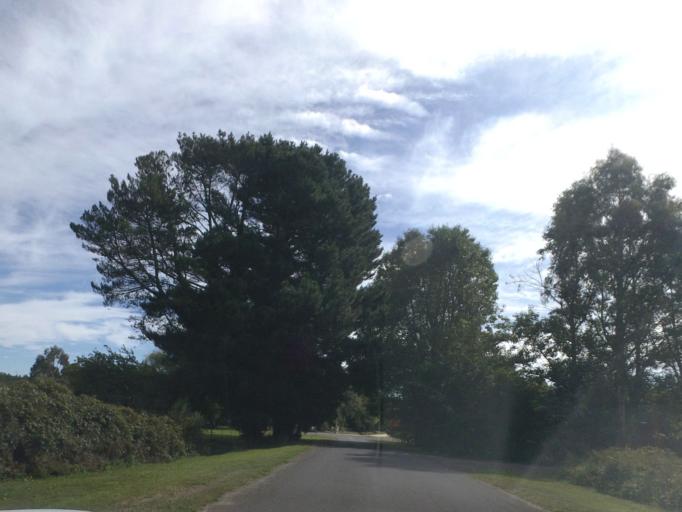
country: AU
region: Victoria
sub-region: Mount Alexander
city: Castlemaine
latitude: -37.3910
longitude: 144.2589
